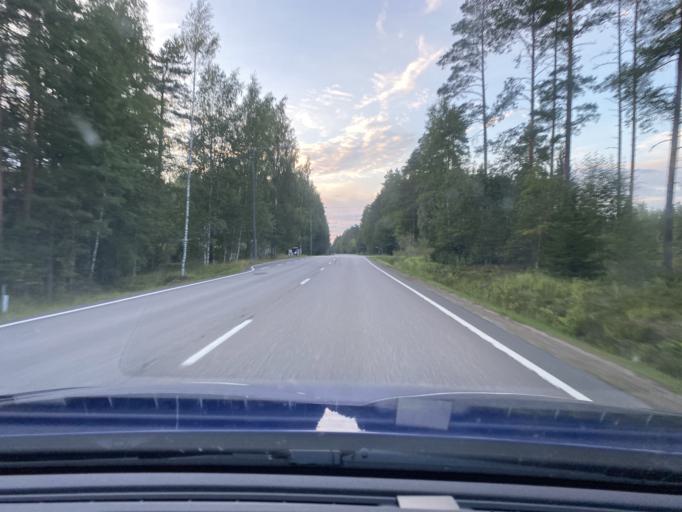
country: FI
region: Satakunta
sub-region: Pohjois-Satakunta
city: Honkajoki
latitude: 61.9548
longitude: 22.2249
